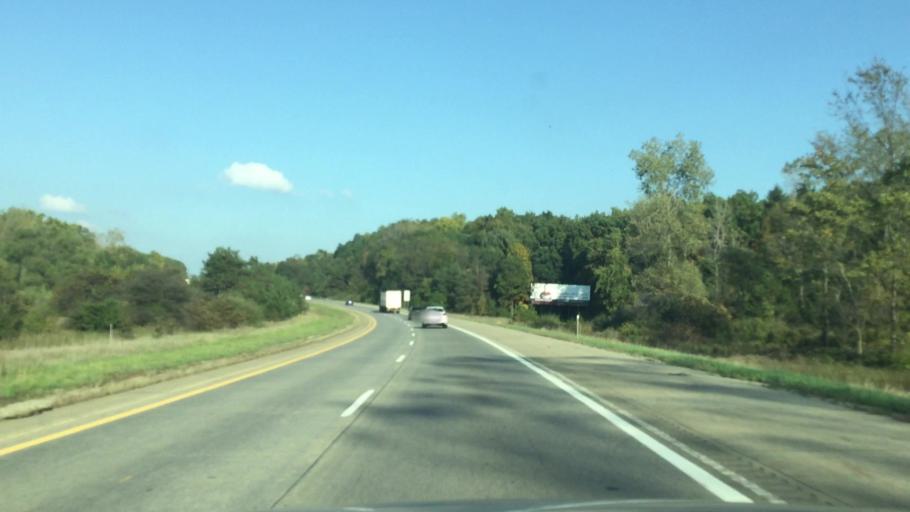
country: US
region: Michigan
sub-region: Jackson County
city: Michigan Center
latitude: 42.2809
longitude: -84.2934
